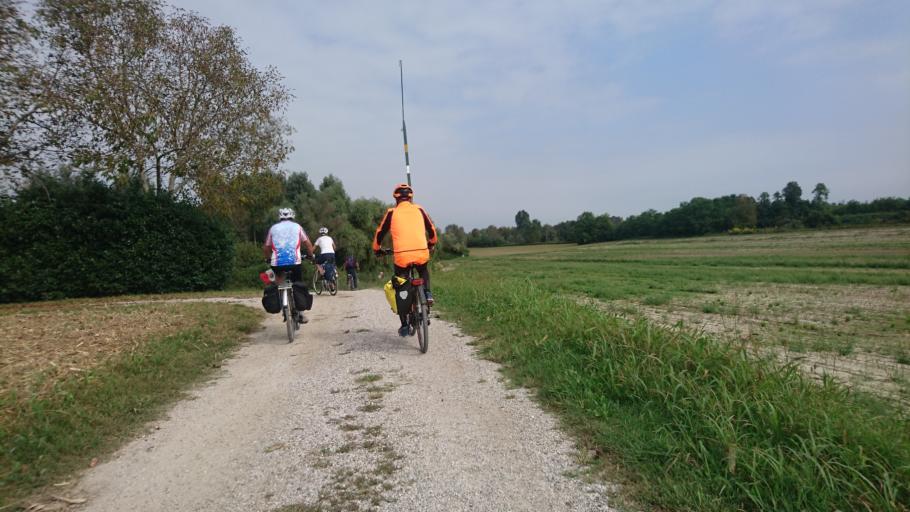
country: IT
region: Veneto
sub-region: Provincia di Padova
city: Piazzola sul Brenta
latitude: 45.5582
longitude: 11.7943
